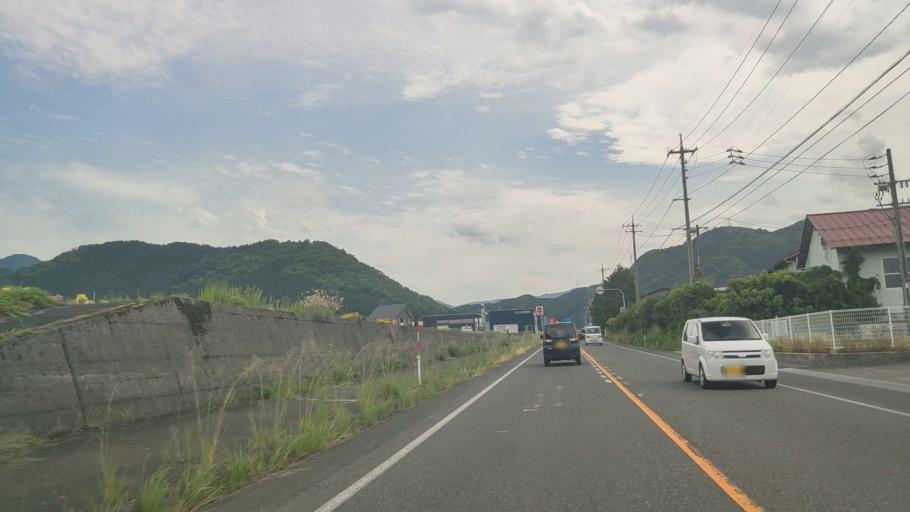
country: JP
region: Tottori
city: Tottori
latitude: 35.3586
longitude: 134.2093
